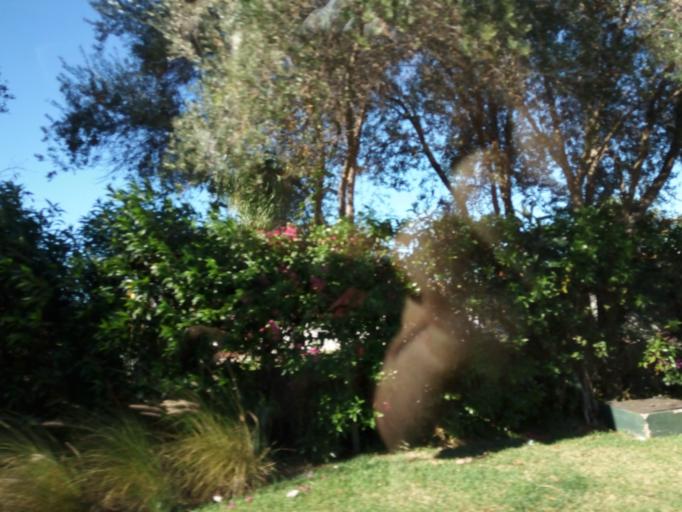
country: PT
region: Faro
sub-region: Loule
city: Vilamoura
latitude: 37.1149
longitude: -8.1181
